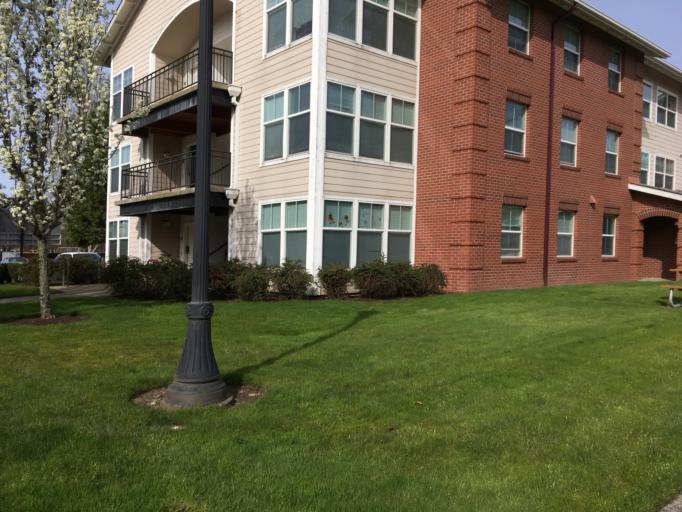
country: US
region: Oregon
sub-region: Yamhill County
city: McMinnville
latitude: 45.1975
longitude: -123.1998
